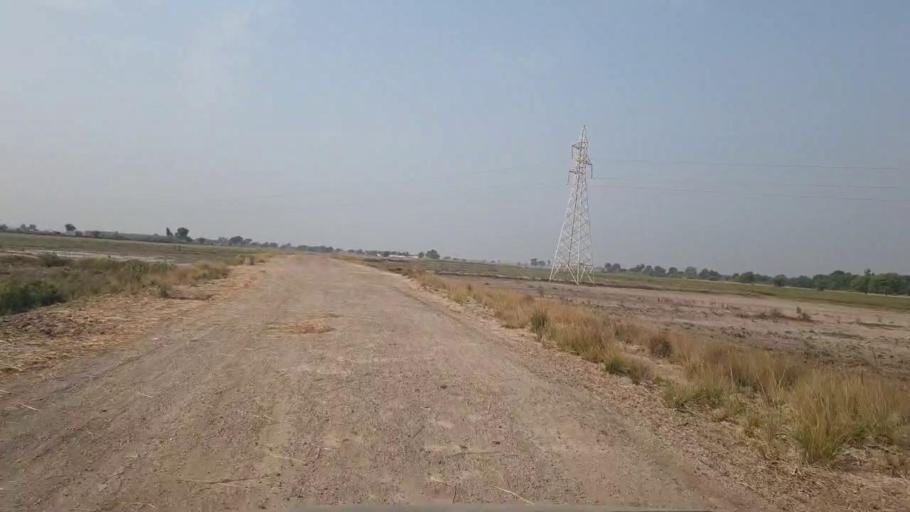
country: PK
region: Sindh
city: Tando Muhammad Khan
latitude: 25.1086
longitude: 68.5118
